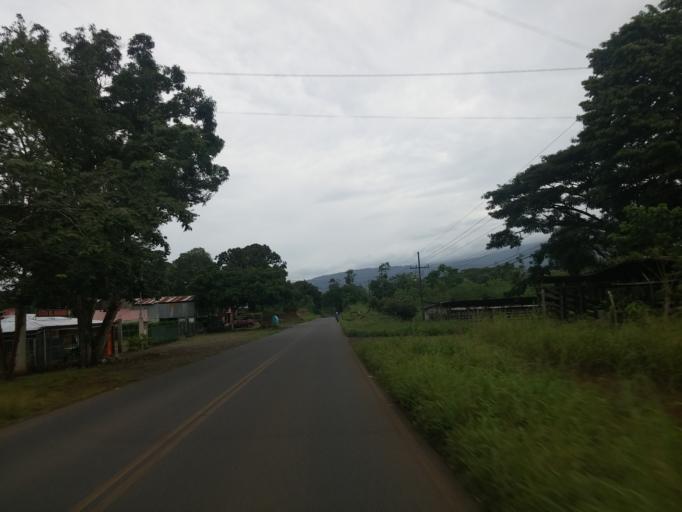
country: CR
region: Alajuela
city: Upala
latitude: 10.8496
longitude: -85.0394
